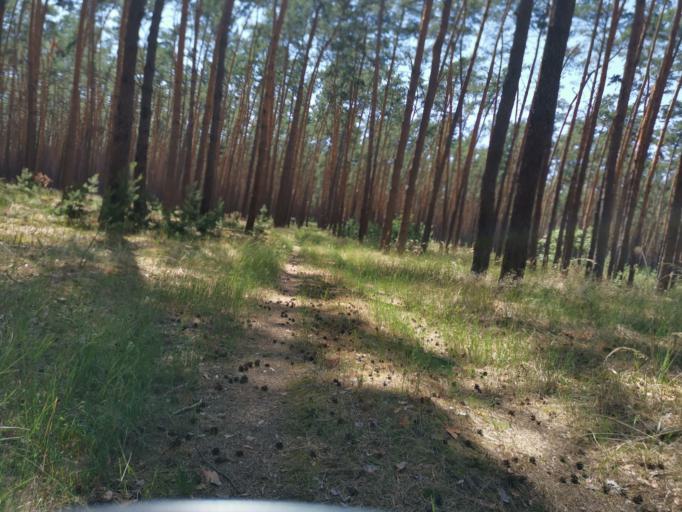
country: CZ
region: South Moravian
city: Petrov
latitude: 48.9199
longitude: 17.2392
